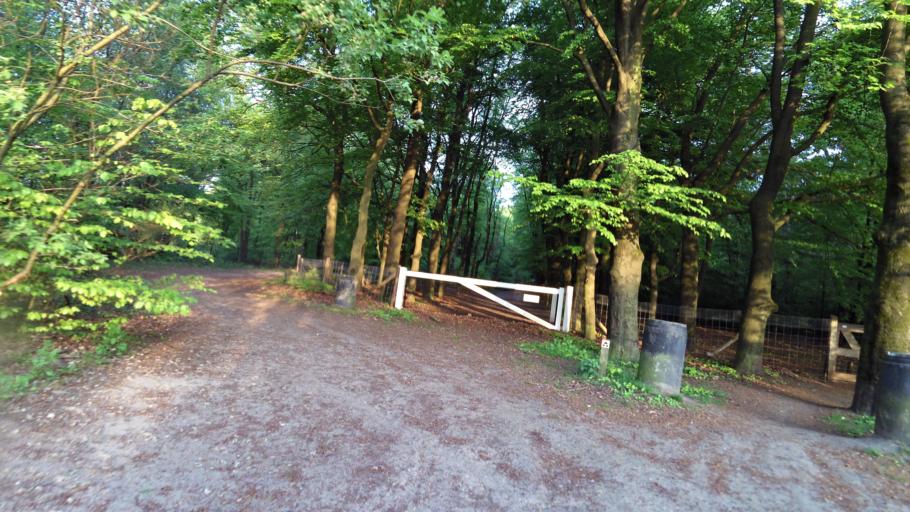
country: NL
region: Gelderland
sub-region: Gemeente Ede
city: Ede
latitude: 52.0359
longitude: 5.6900
